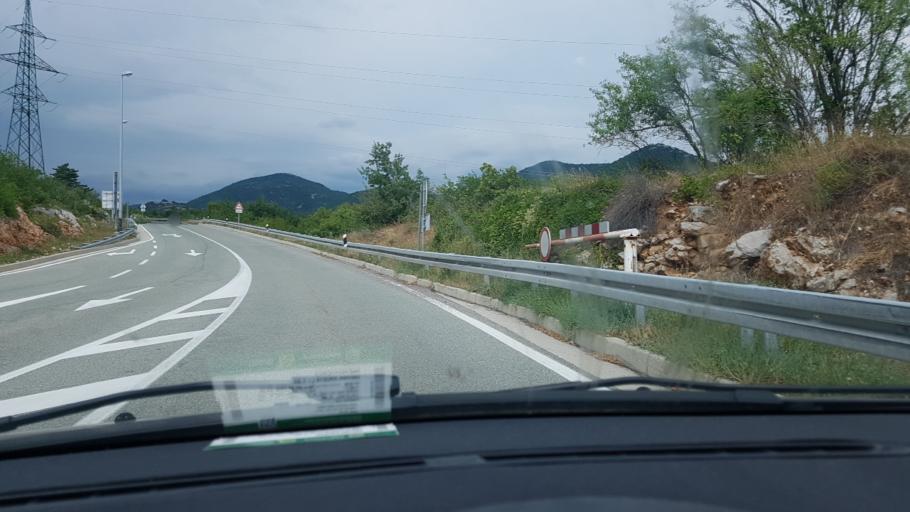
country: HR
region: Primorsko-Goranska
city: Hreljin
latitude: 45.2937
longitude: 14.5872
